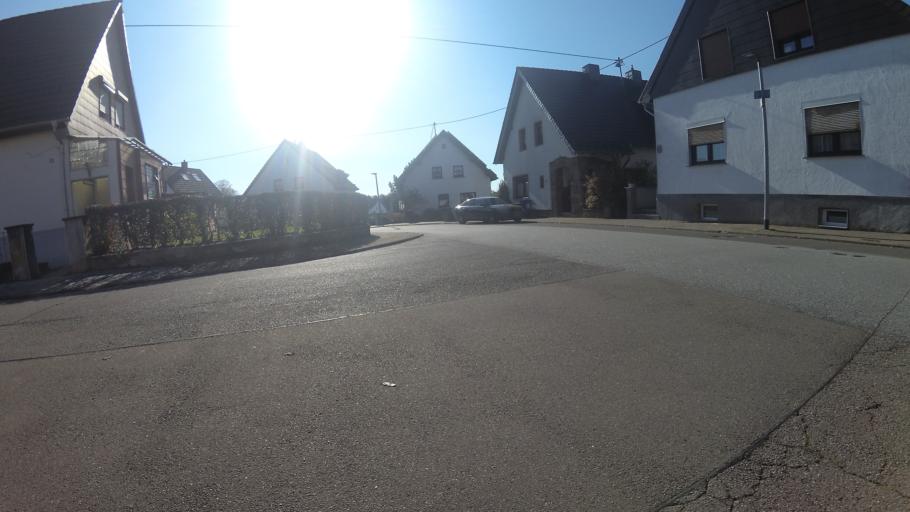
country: DE
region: Saarland
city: Neunkirchen
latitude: 49.3438
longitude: 7.1987
